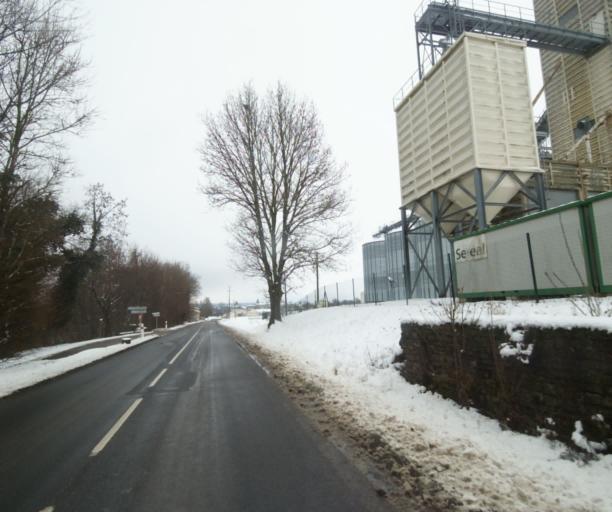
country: FR
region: Champagne-Ardenne
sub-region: Departement de la Haute-Marne
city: Wassy
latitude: 48.4336
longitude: 4.9617
